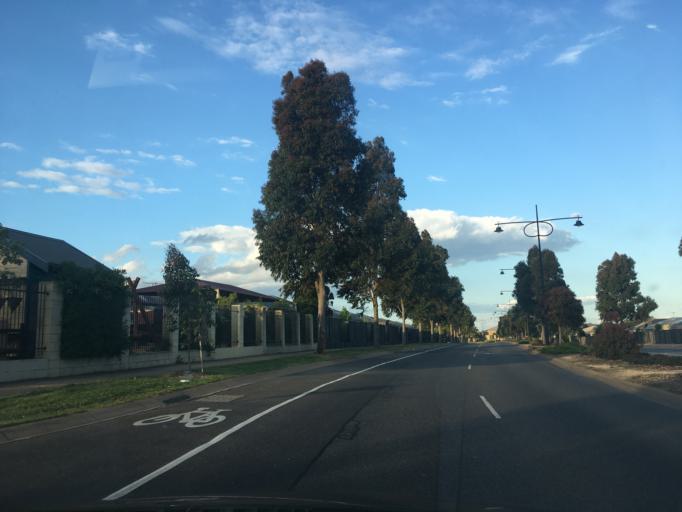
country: AU
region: Victoria
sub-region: Wyndham
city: Hoppers Crossing
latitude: -37.8920
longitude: 144.7293
